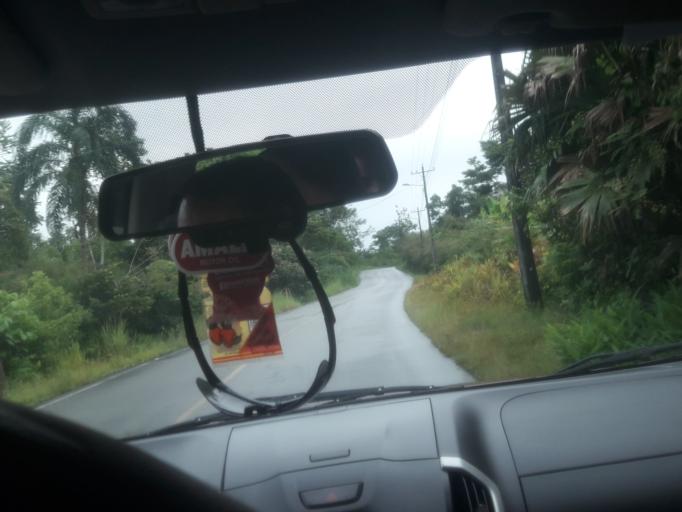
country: EC
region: Napo
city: Tena
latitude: -1.0344
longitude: -77.7241
